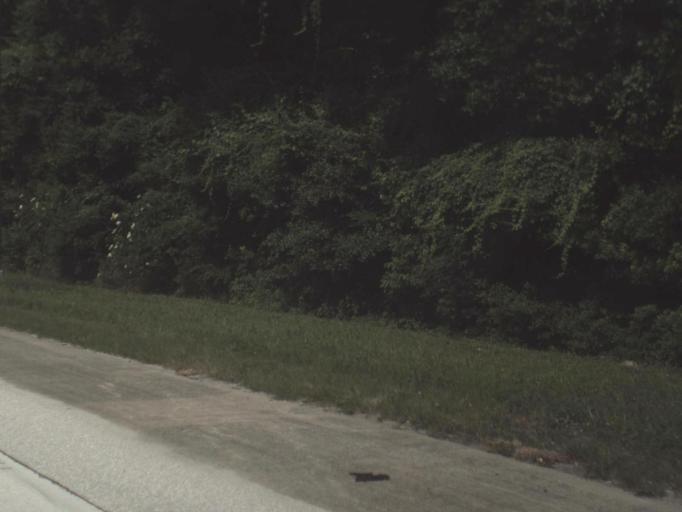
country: US
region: Florida
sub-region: Saint Johns County
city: Fruit Cove
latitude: 30.1924
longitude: -81.5566
